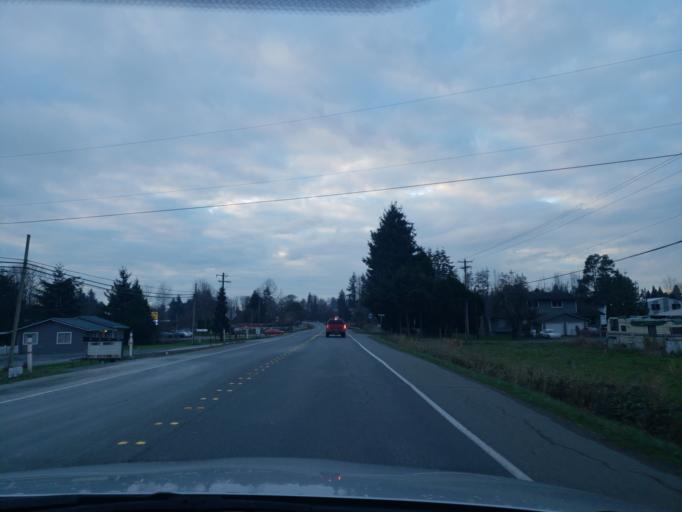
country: US
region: Washington
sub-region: Snohomish County
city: Snohomish
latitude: 47.9132
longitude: -122.0775
